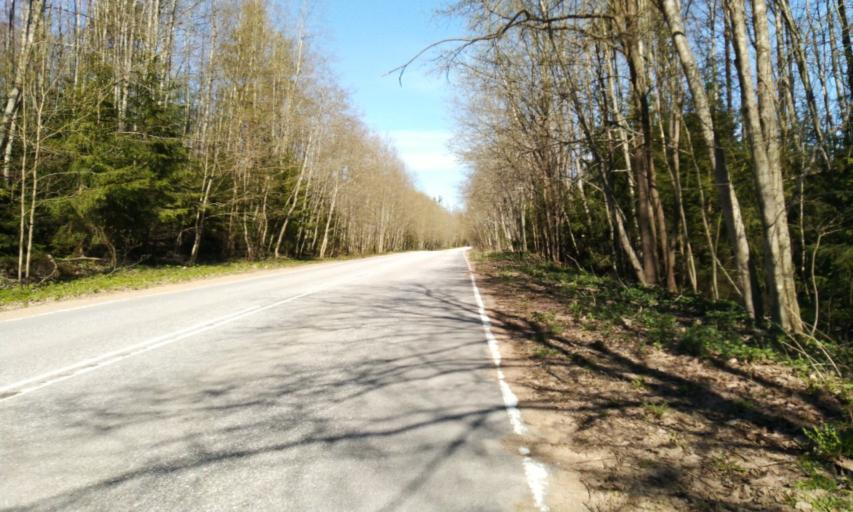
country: RU
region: Leningrad
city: Garbolovo
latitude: 60.4071
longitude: 30.4647
